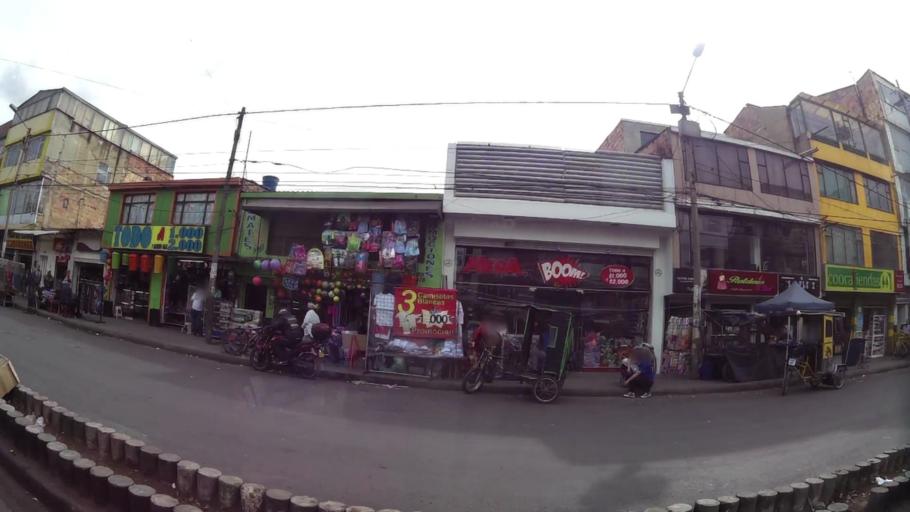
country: CO
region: Cundinamarca
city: Soacha
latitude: 4.6357
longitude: -74.1639
